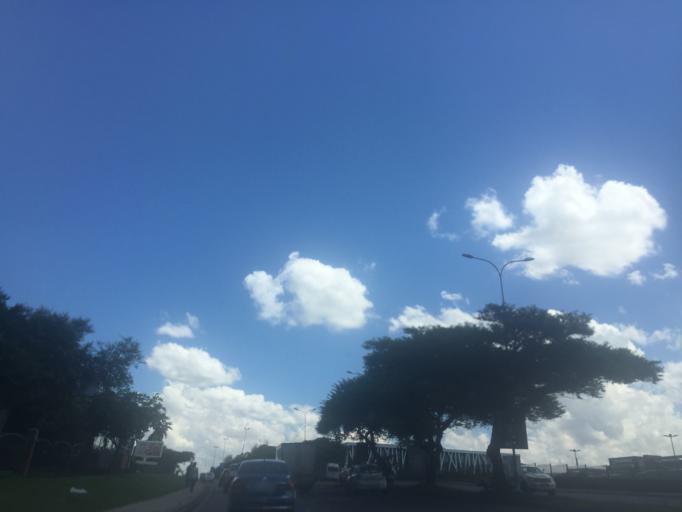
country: ZA
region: Gauteng
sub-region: City of Johannesburg Metropolitan Municipality
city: Diepsloot
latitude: -26.0522
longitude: 28.0214
